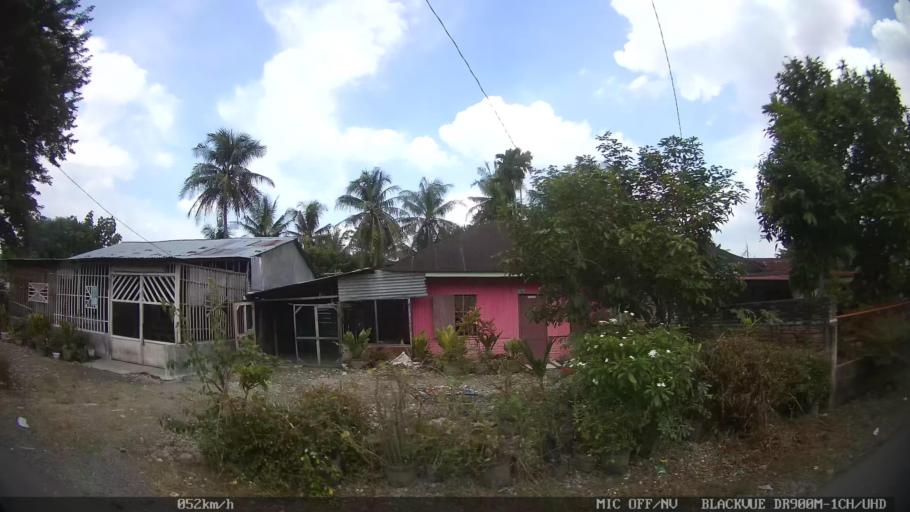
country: ID
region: North Sumatra
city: Binjai
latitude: 3.6350
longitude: 98.5174
